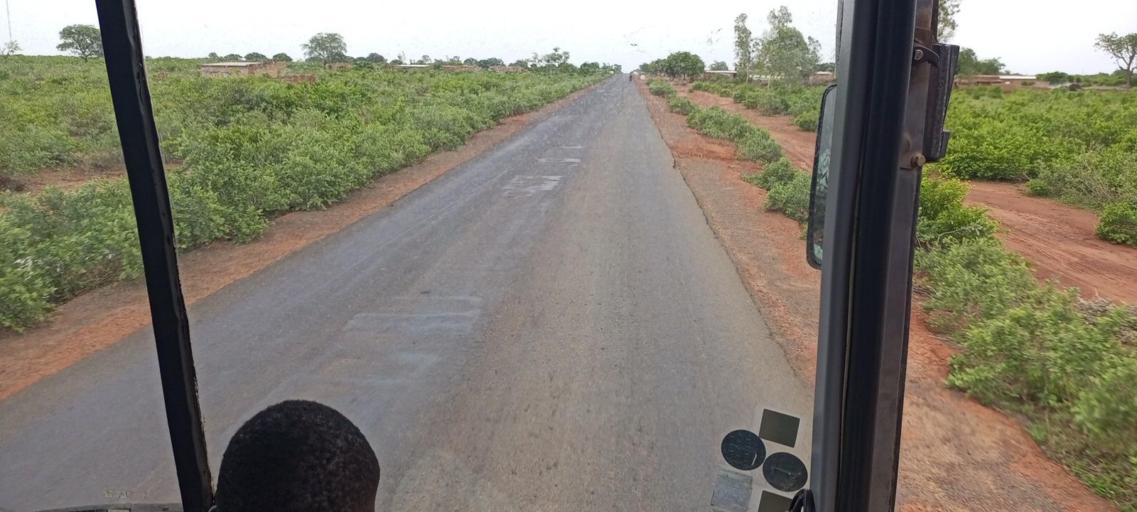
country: ML
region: Sikasso
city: Koutiala
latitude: 12.5381
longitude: -5.5732
